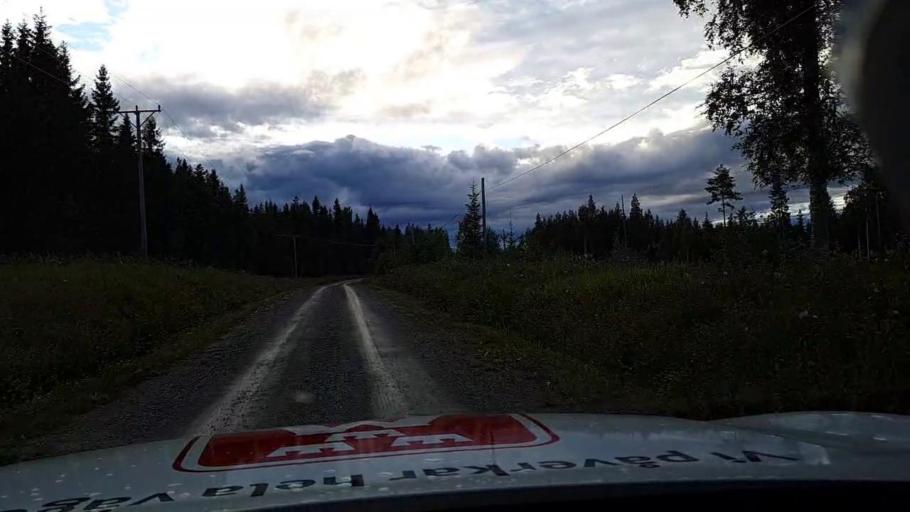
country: SE
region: Jaemtland
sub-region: Bergs Kommun
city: Hoverberg
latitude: 62.8748
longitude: 14.6131
